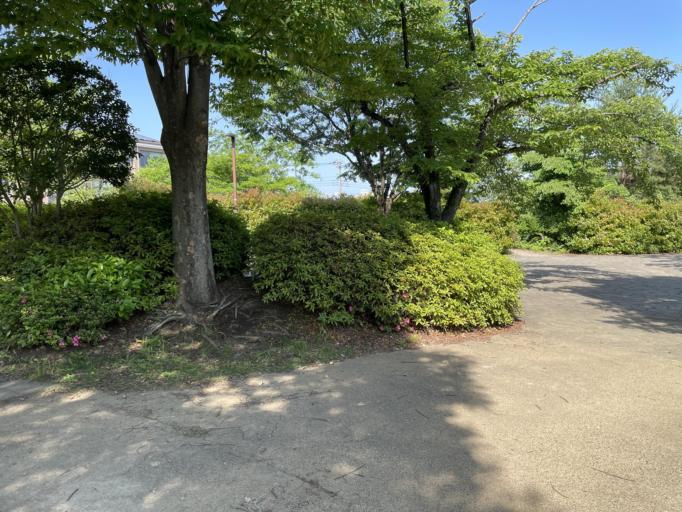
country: JP
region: Saitama
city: Hanno
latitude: 35.8450
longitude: 139.3074
